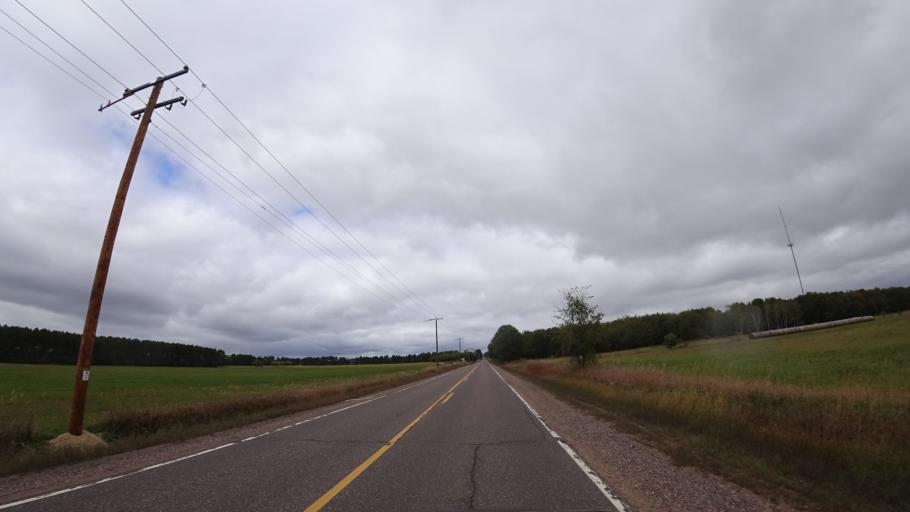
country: US
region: Wisconsin
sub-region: Chippewa County
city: Lake Wissota
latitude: 44.9736
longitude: -91.2678
